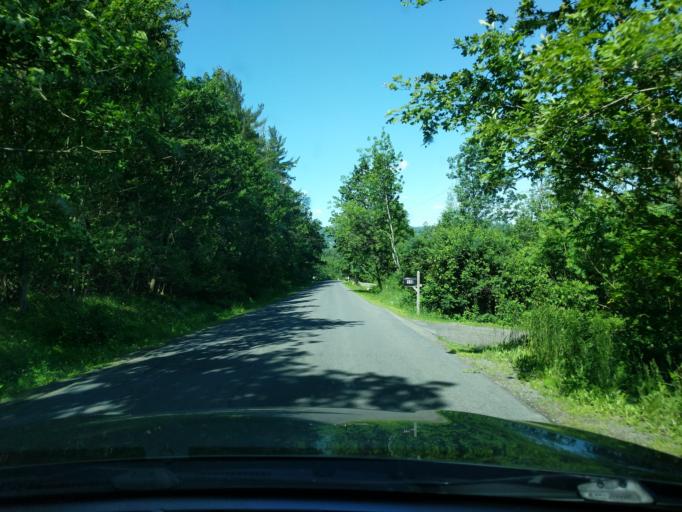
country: US
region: New York
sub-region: Tompkins County
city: East Ithaca
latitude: 42.3807
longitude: -76.3708
